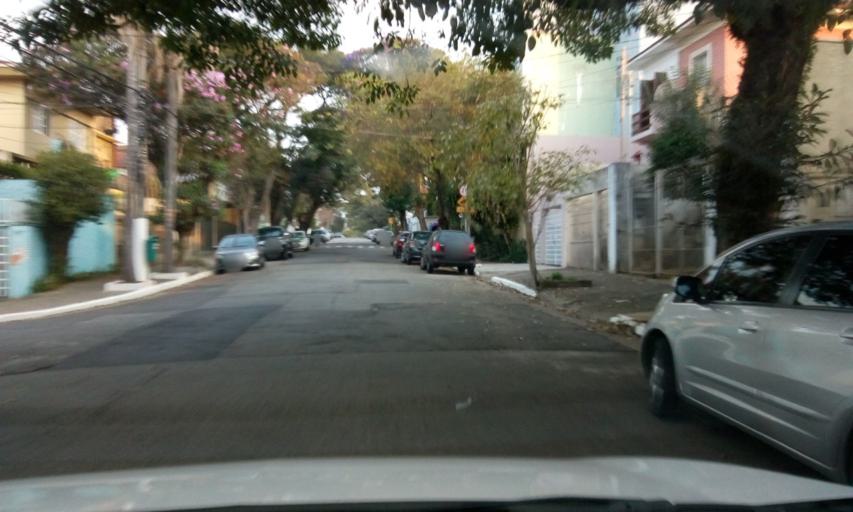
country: BR
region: Sao Paulo
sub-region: Sao Paulo
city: Sao Paulo
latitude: -23.6091
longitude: -46.6485
